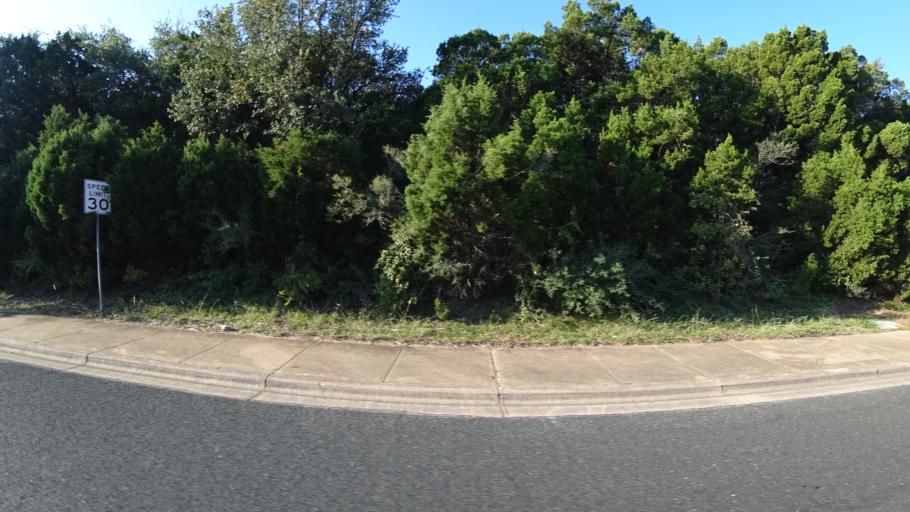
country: US
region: Texas
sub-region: Travis County
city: Rollingwood
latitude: 30.2617
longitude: -97.8087
